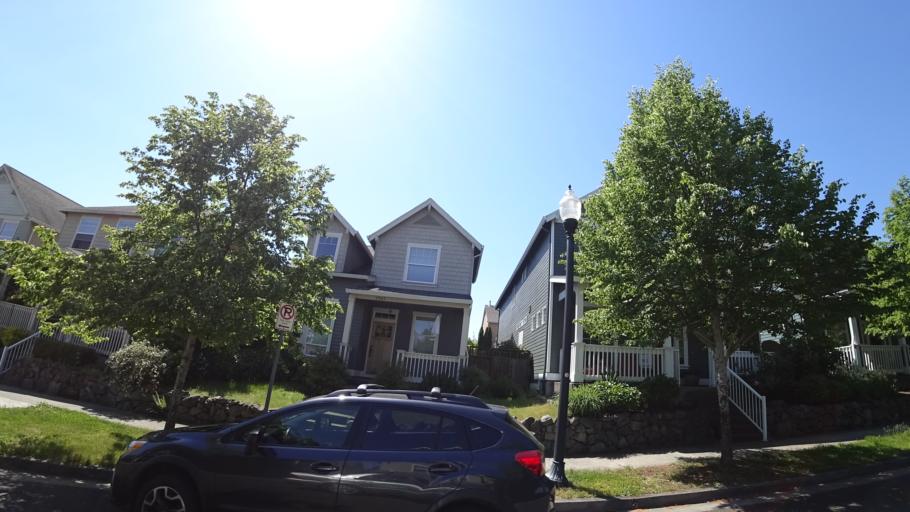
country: US
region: Oregon
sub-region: Washington County
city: Cedar Hills
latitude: 45.4956
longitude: -122.7976
